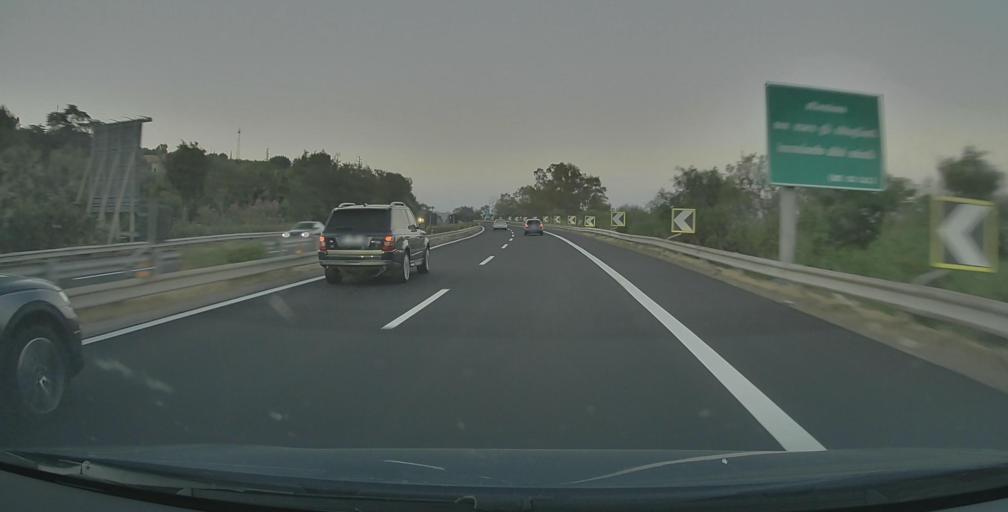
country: IT
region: Sicily
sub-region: Messina
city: Roccalumera
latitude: 37.9725
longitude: 15.3899
